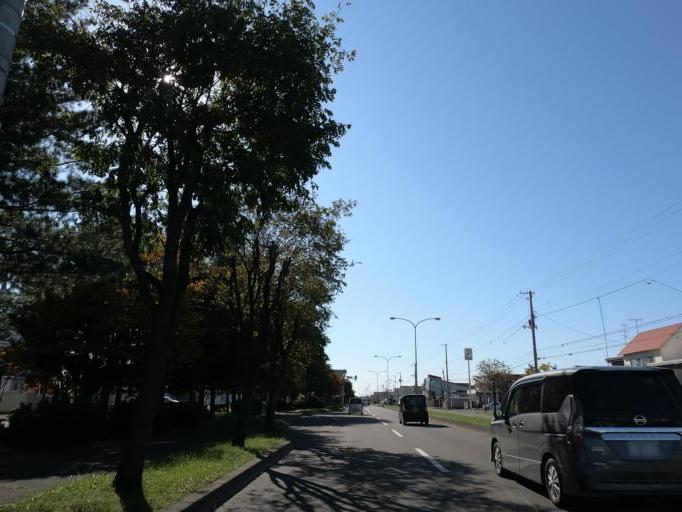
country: JP
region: Hokkaido
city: Obihiro
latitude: 42.9098
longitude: 143.2142
